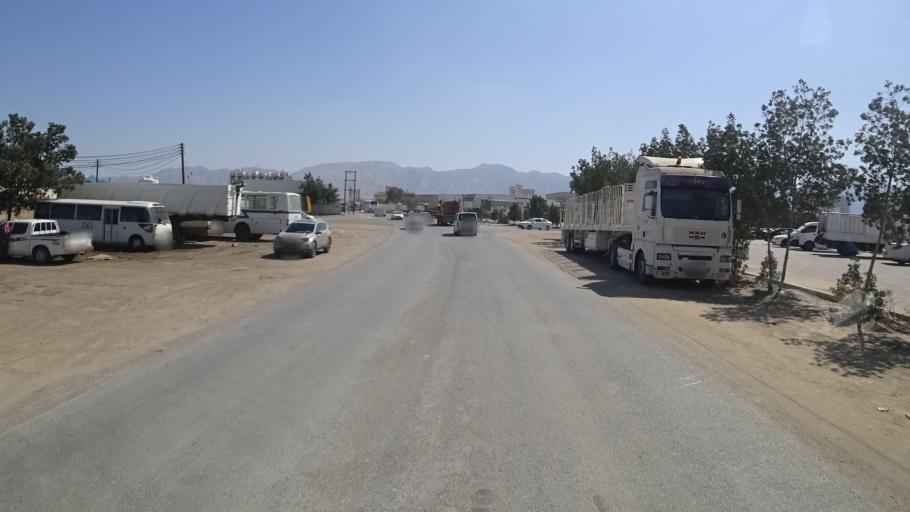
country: OM
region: Muhafazat Masqat
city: Bawshar
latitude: 23.5766
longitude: 58.3669
